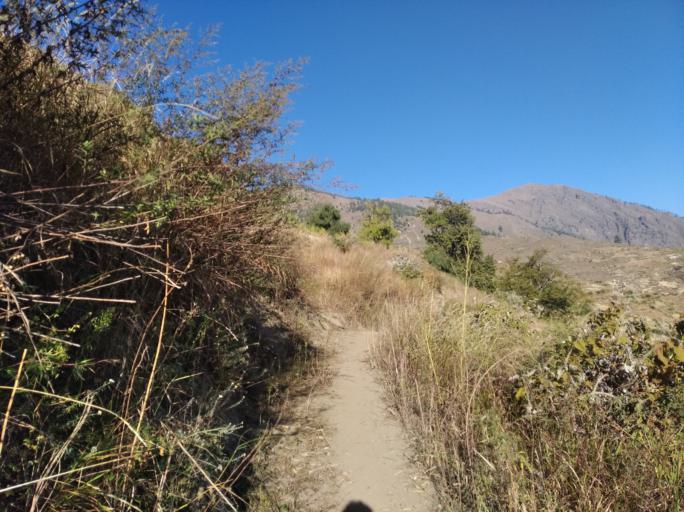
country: NP
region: Western Region
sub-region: Dhawalagiri Zone
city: Jomsom
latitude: 28.8803
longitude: 82.9835
